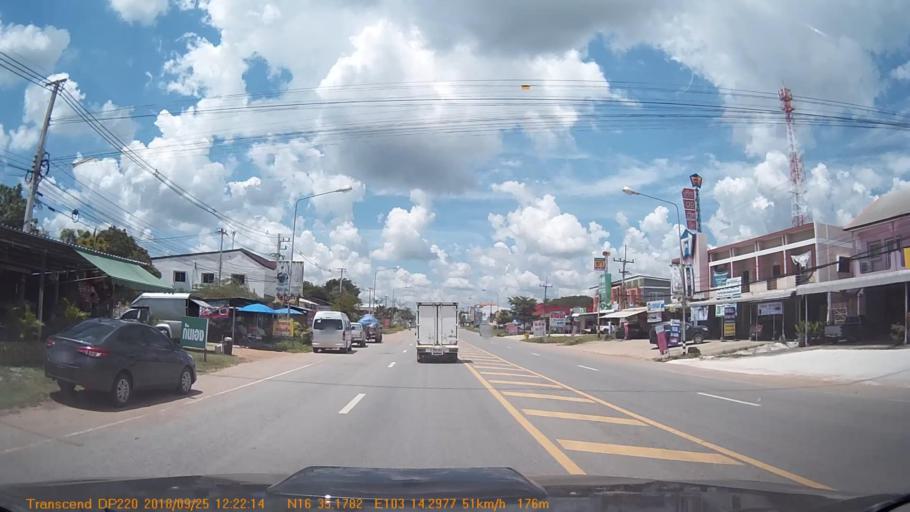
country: TH
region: Kalasin
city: Huai Mek
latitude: 16.5862
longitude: 103.2384
